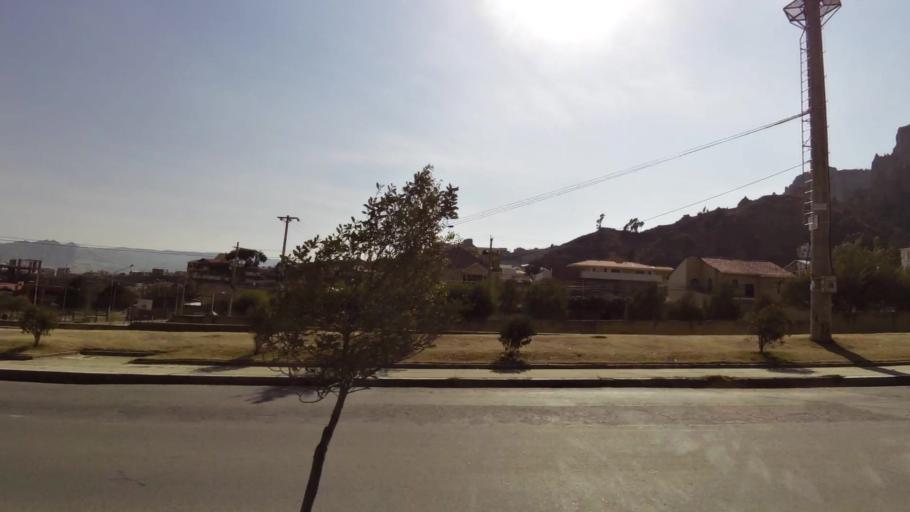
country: BO
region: La Paz
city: La Paz
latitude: -16.5255
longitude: -68.0679
